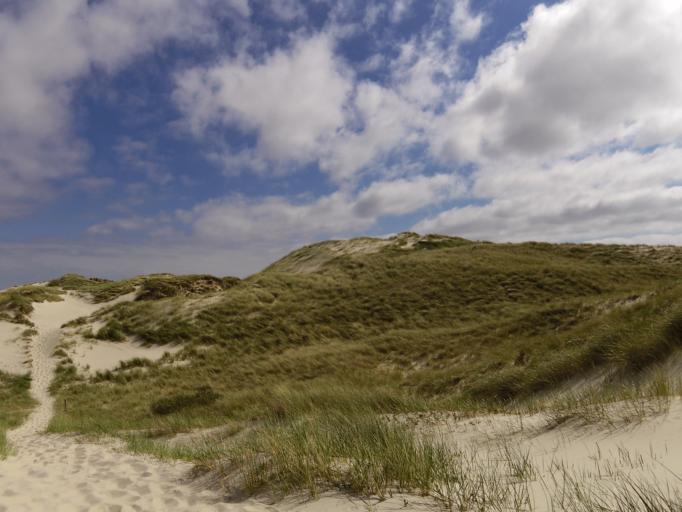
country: DE
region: Schleswig-Holstein
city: Nebel
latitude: 54.6239
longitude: 8.3581
